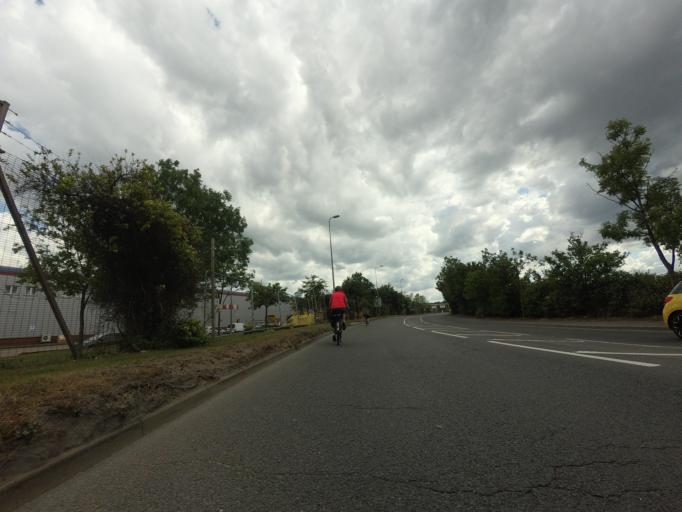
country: GB
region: England
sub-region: Medway
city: Rochester
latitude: 51.3964
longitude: 0.5177
